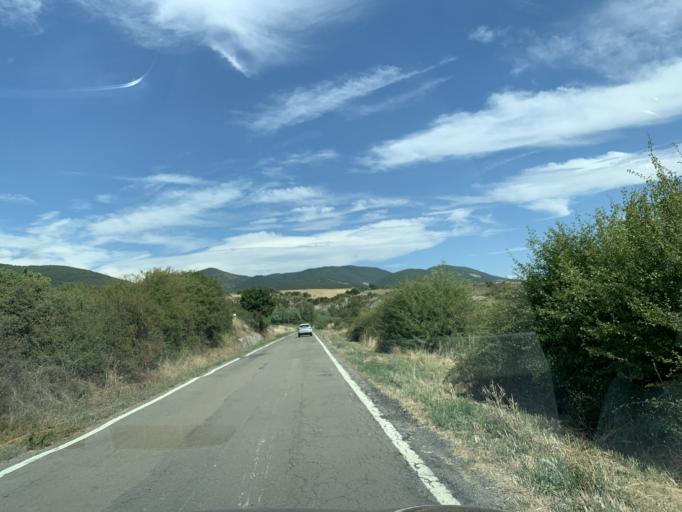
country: ES
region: Aragon
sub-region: Provincia de Huesca
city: Santa Cruz de la Seros
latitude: 42.5931
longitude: -0.6410
